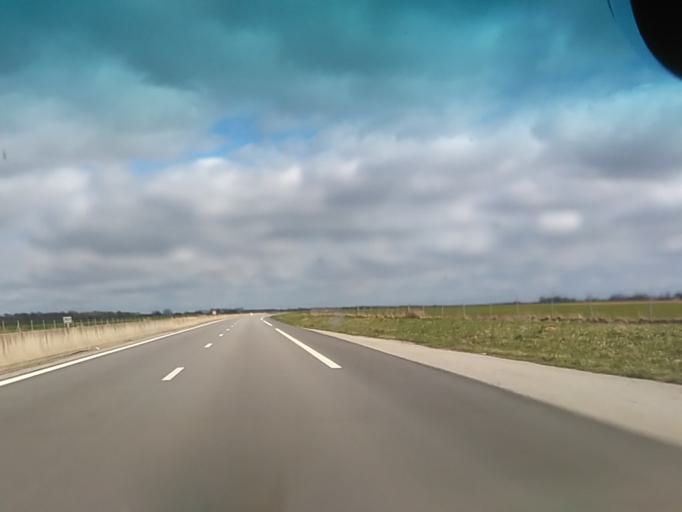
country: FR
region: Haute-Normandie
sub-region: Departement de l'Eure
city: Menneval
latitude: 49.1551
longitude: 0.6318
